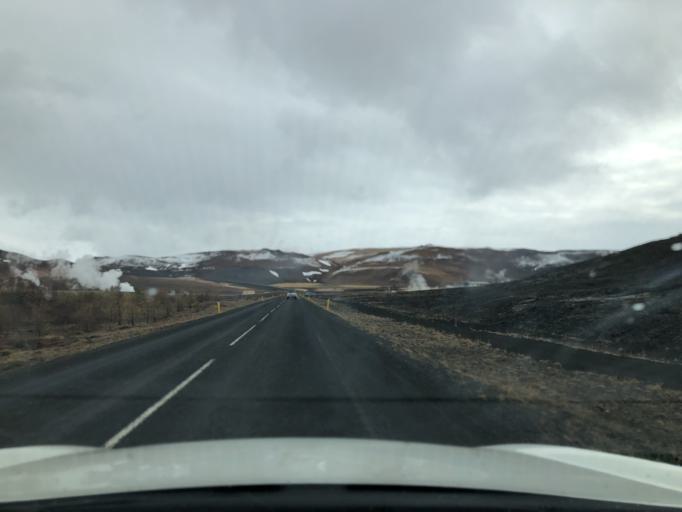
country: IS
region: Northeast
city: Laugar
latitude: 65.6395
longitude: -16.8595
